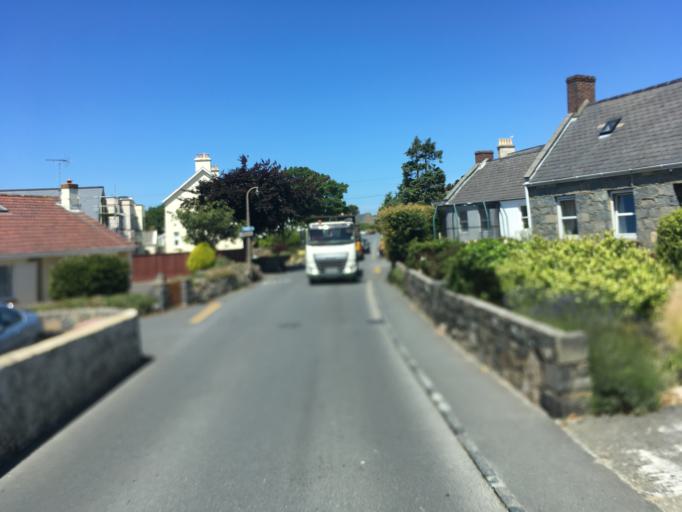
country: GG
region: St Peter Port
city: Saint Peter Port
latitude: 49.4975
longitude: -2.5096
